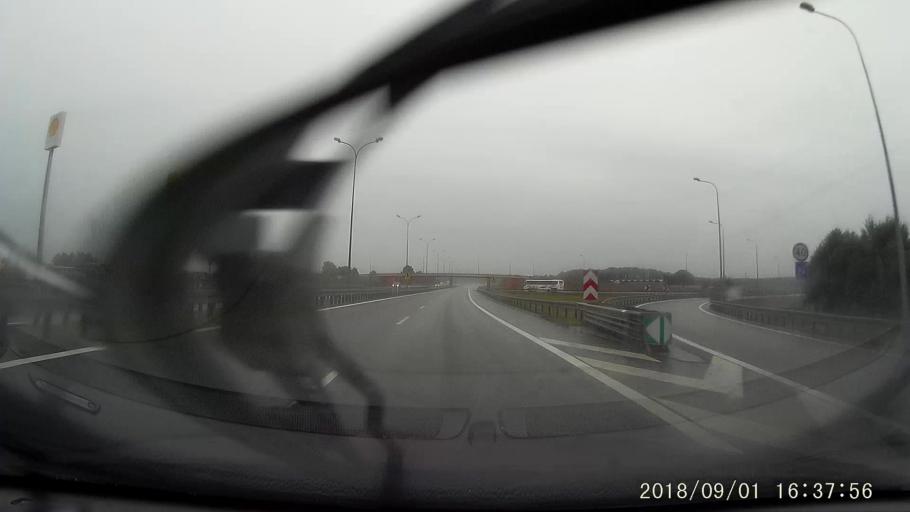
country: PL
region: Lubusz
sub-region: Powiat zielonogorski
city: Sulechow
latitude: 52.0660
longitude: 15.6145
